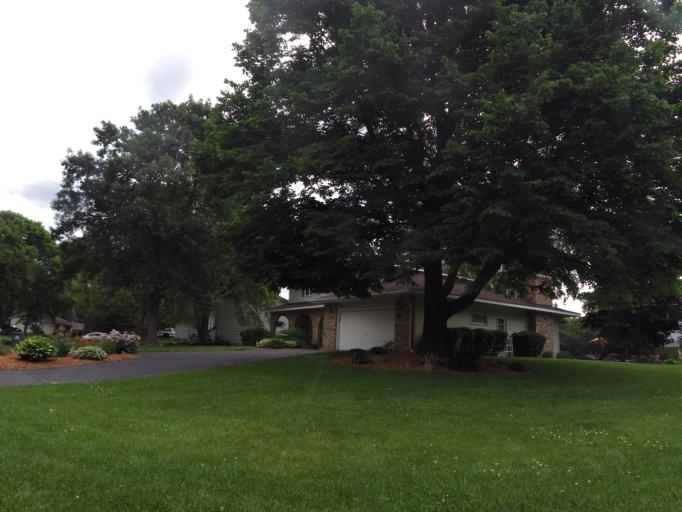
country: US
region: Minnesota
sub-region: Scott County
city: Prior Lake
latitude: 44.7061
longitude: -93.4476
